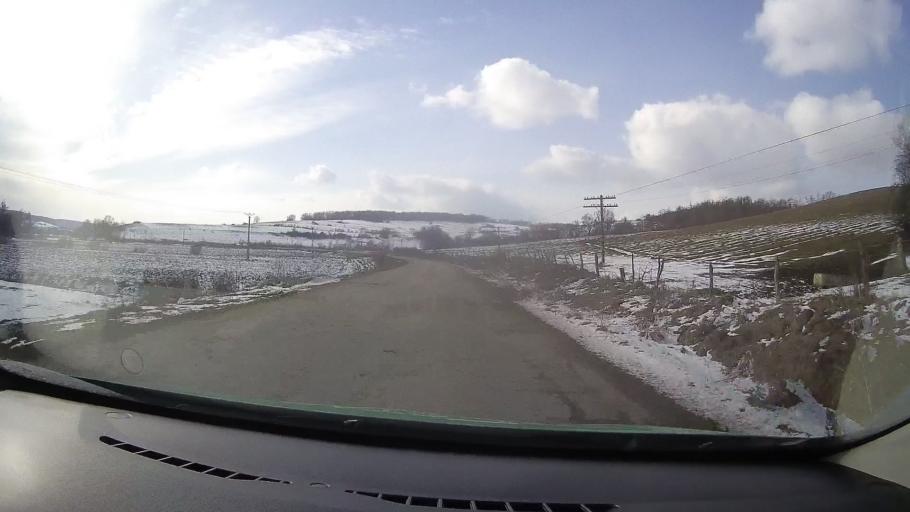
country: RO
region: Sibiu
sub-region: Comuna Iacobeni
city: Iacobeni
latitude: 46.0501
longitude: 24.7690
